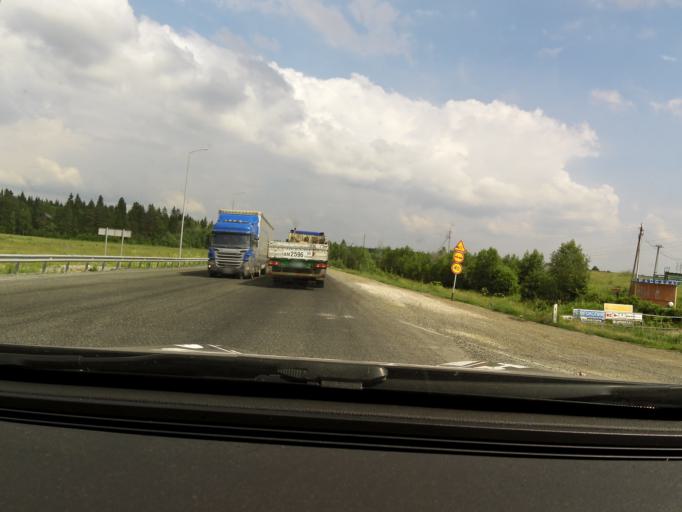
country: RU
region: Sverdlovsk
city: Ufimskiy
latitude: 56.7628
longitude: 58.1491
